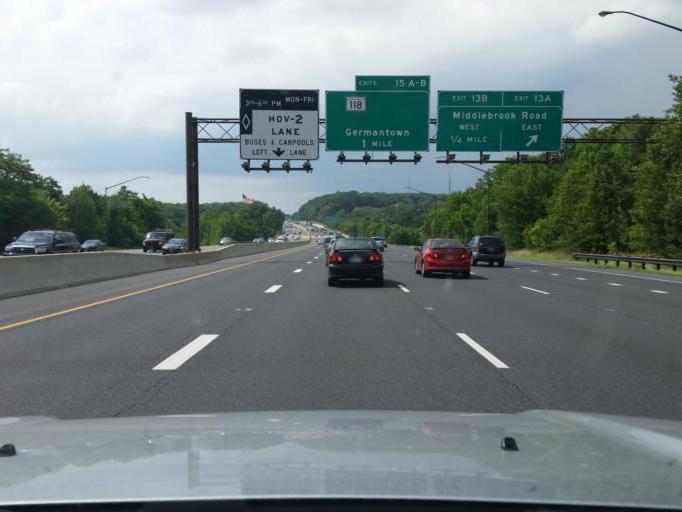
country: US
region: Maryland
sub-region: Montgomery County
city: Germantown
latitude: 39.1719
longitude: -77.2446
